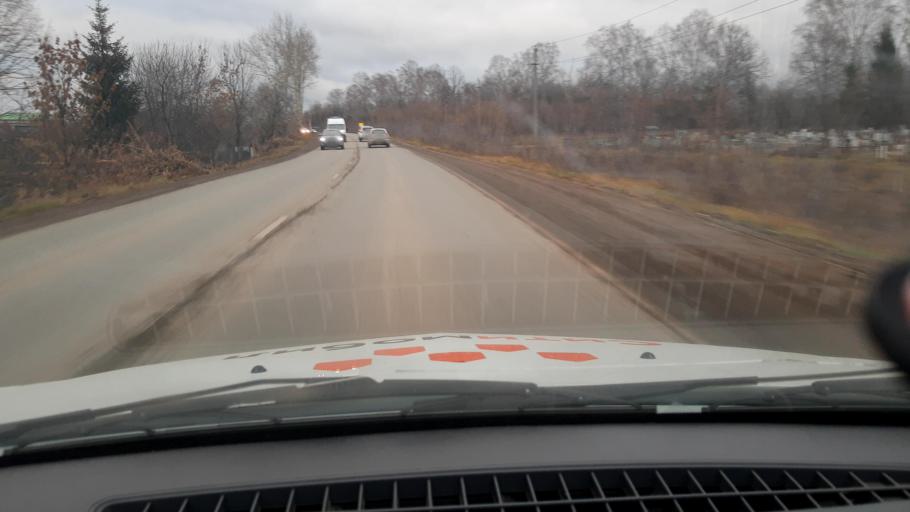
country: RU
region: Bashkortostan
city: Iglino
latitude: 54.7953
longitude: 56.3021
